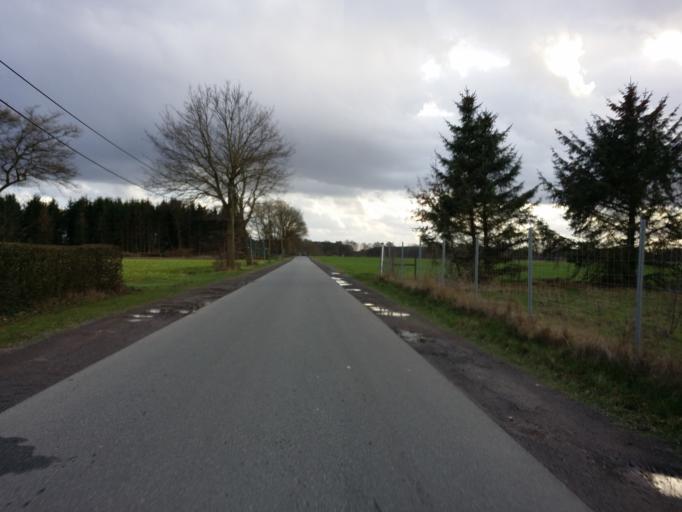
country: DE
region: Lower Saxony
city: Delmenhorst
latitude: 53.0060
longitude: 8.6486
